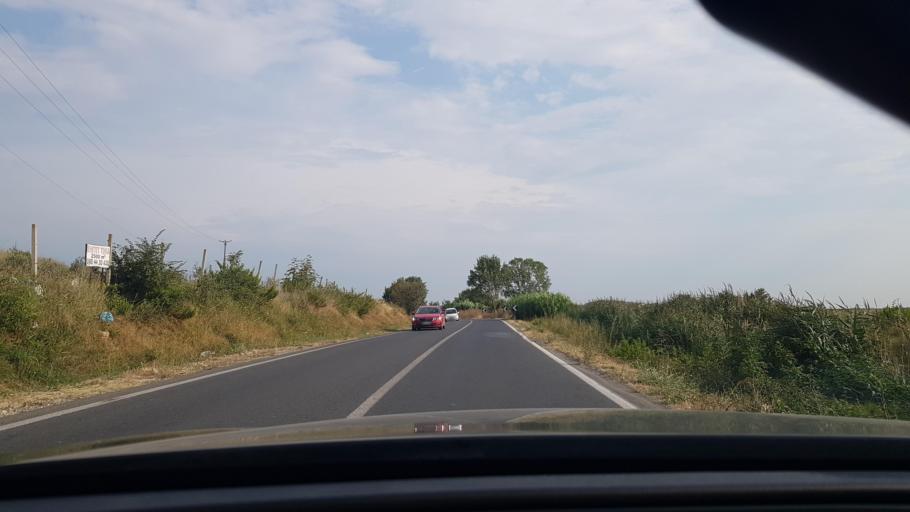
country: AL
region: Durres
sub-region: Rrethi i Durresit
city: Manze
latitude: 41.4598
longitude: 19.5648
